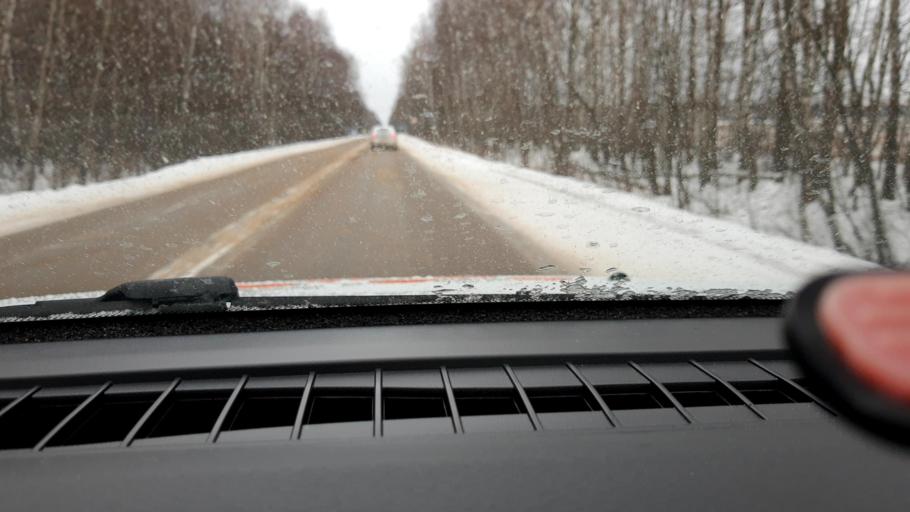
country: RU
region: Nizjnij Novgorod
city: Kstovo
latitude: 56.2965
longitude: 44.2732
